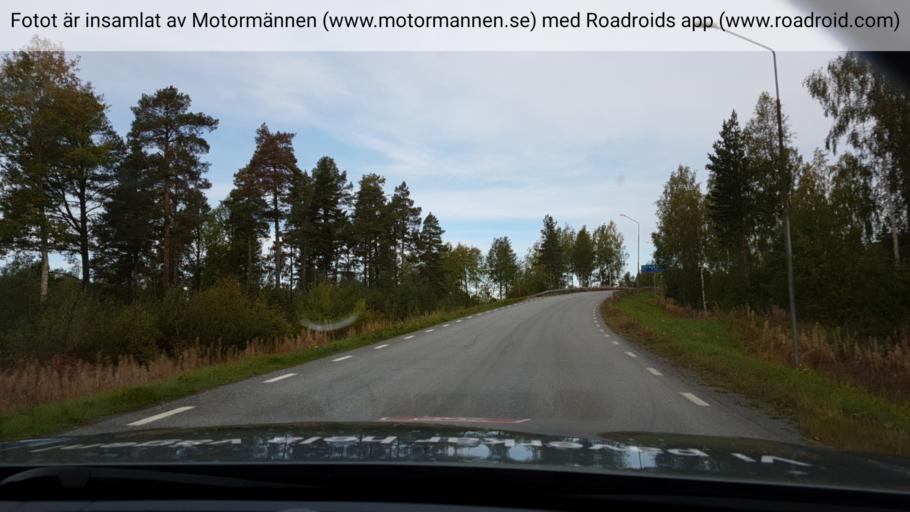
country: SE
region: Jaemtland
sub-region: Krokoms Kommun
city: Krokom
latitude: 63.3146
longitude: 14.1775
